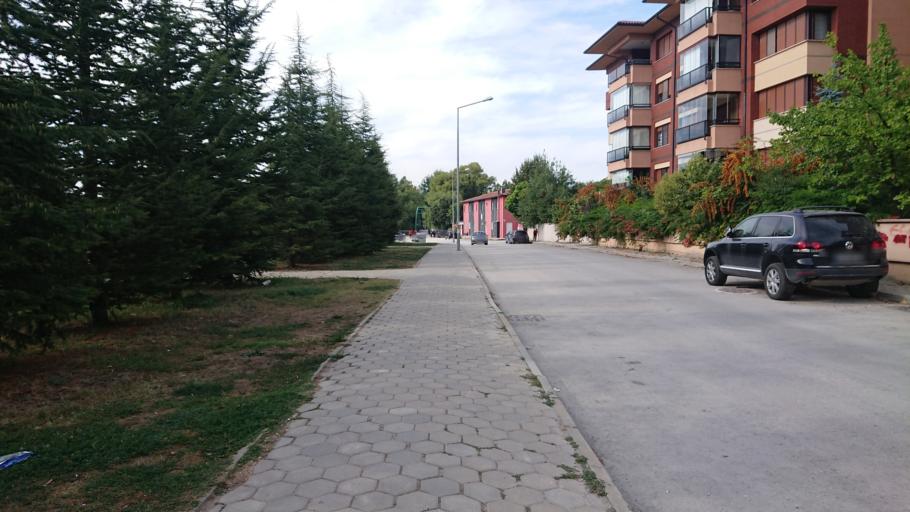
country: TR
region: Eskisehir
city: Eskisehir
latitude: 39.7675
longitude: 30.4965
